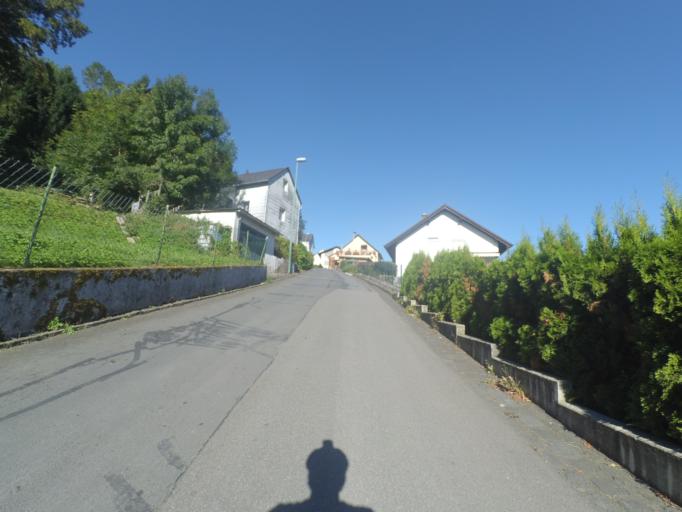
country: DE
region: Rheinland-Pfalz
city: Daun
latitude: 50.1975
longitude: 6.8330
